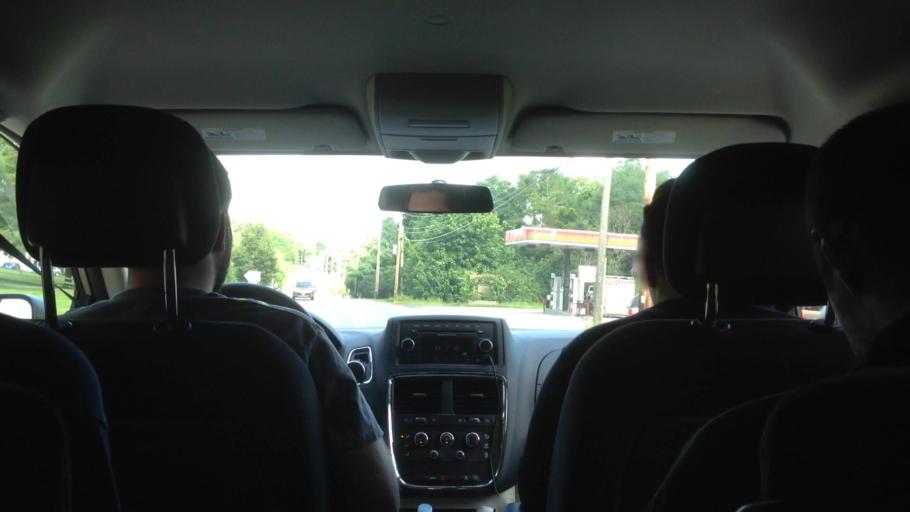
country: US
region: New York
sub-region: Dutchess County
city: Red Hook
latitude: 42.0250
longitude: -73.8478
